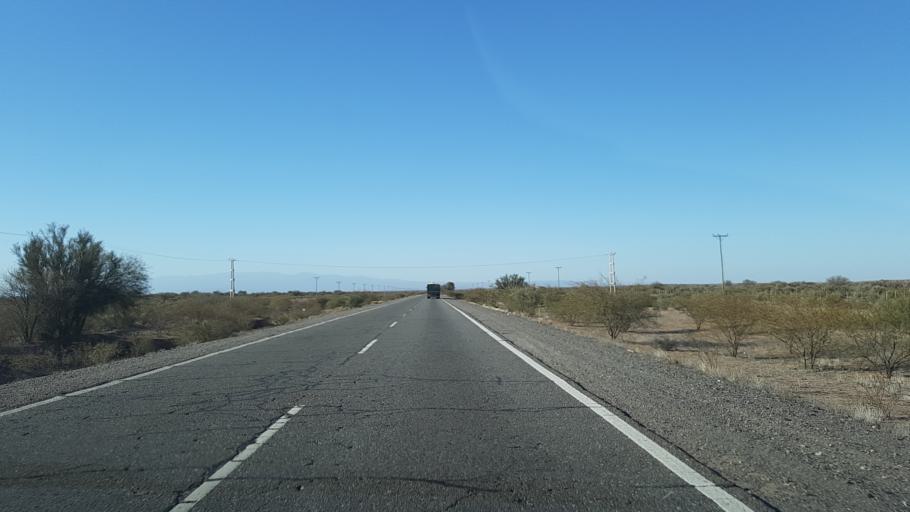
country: AR
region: San Juan
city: Caucete
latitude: -31.6590
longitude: -67.7742
